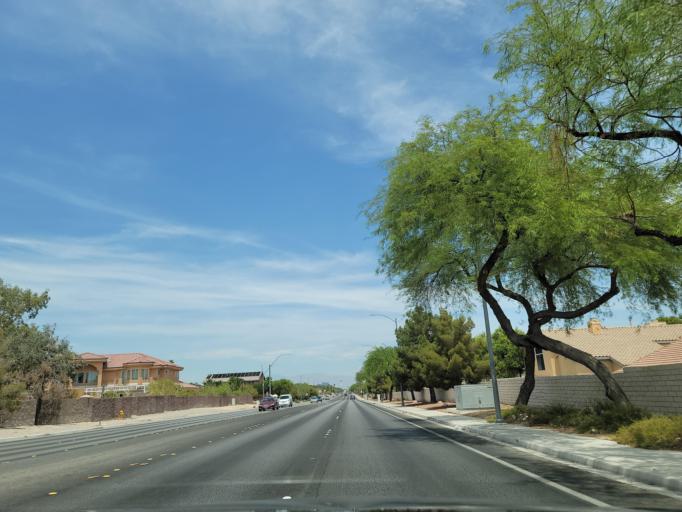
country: US
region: Nevada
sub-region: Clark County
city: Paradise
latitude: 36.0337
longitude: -115.1544
